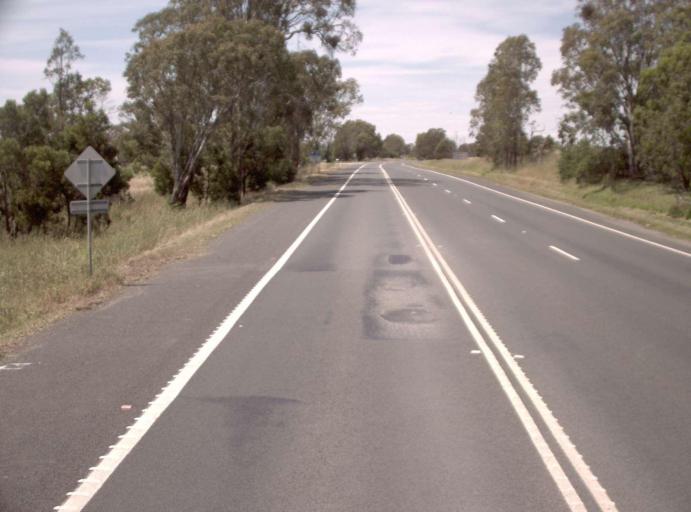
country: AU
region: Victoria
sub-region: Latrobe
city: Traralgon
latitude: -38.1604
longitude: 146.7064
